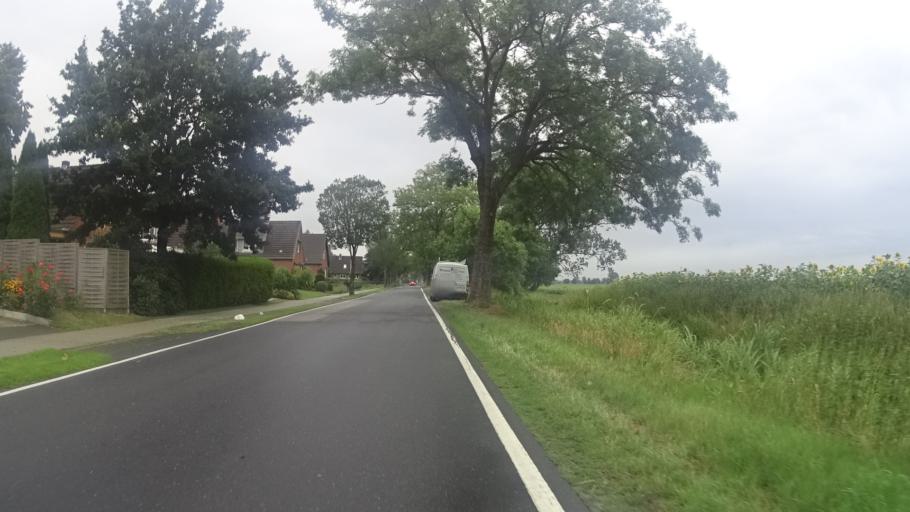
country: DE
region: Schleswig-Holstein
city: Altenmoor
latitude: 53.7843
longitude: 9.5638
